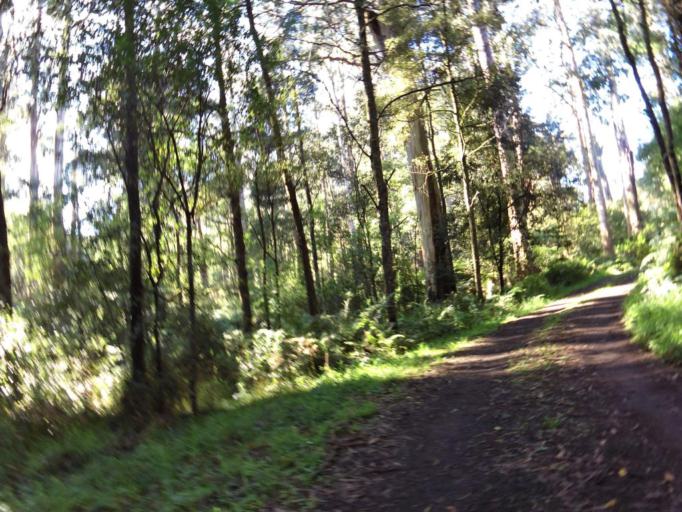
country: AU
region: Victoria
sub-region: Yarra Ranges
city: Monbulk
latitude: -37.8829
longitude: 145.4068
